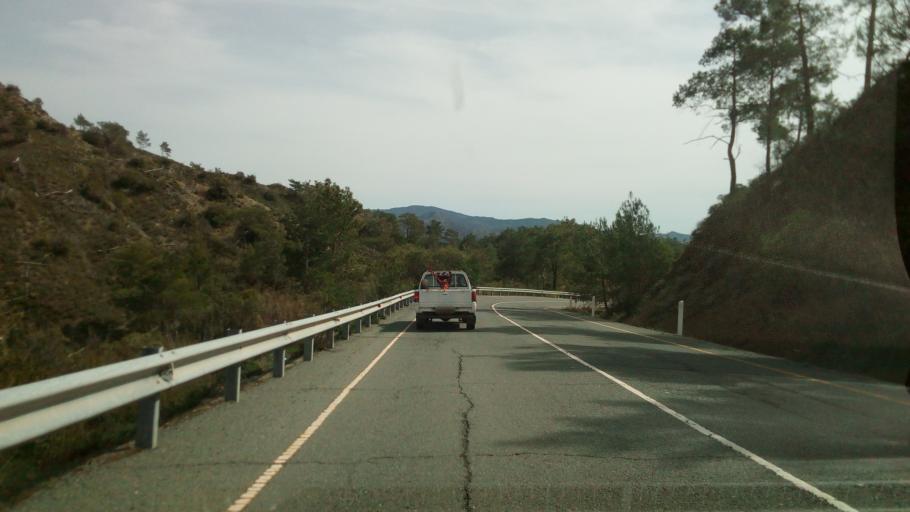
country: CY
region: Limassol
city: Pelendri
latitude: 34.8693
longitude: 32.9302
